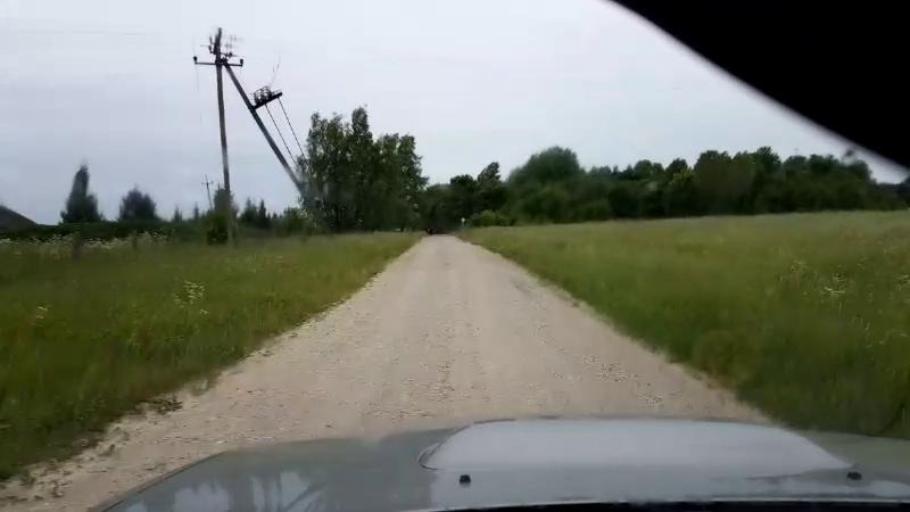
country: EE
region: Paernumaa
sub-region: Halinga vald
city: Parnu-Jaagupi
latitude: 58.5316
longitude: 24.5889
